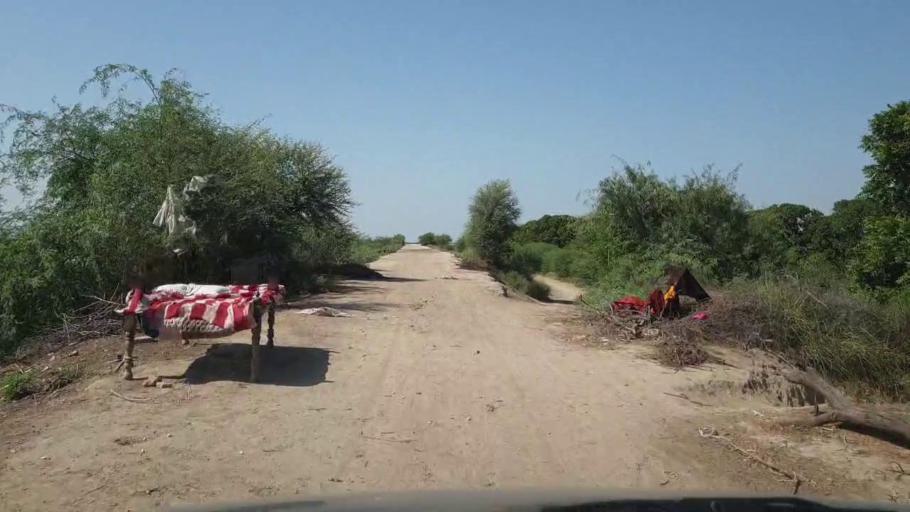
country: PK
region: Sindh
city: Matiari
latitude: 25.6343
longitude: 68.4885
